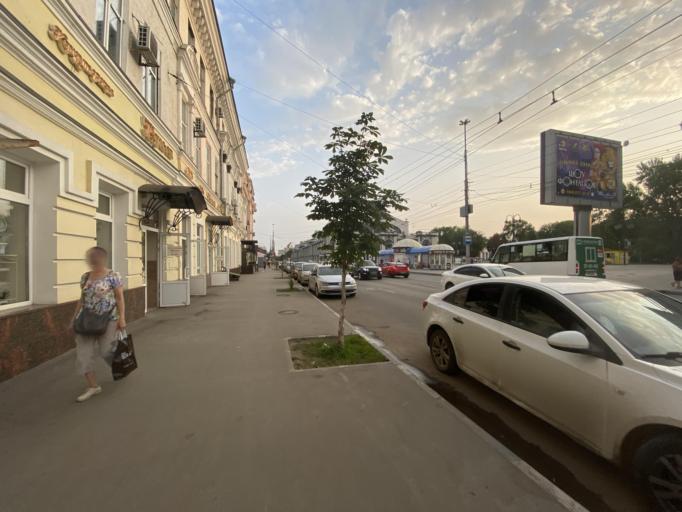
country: RU
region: Saratov
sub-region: Saratovskiy Rayon
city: Saratov
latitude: 51.5336
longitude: 46.0215
